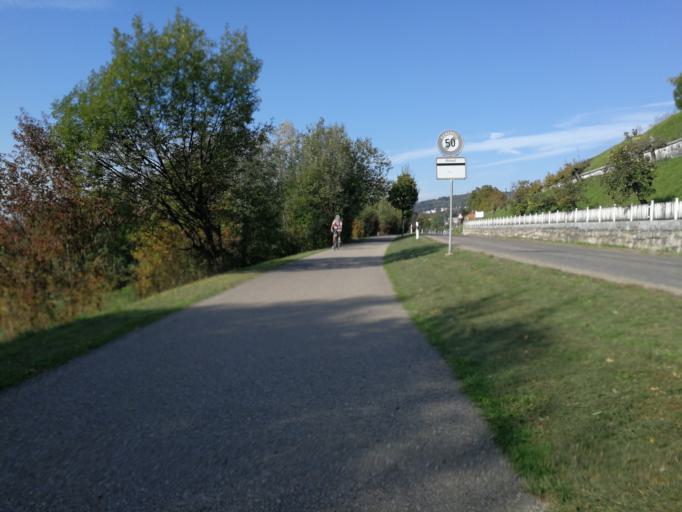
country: CH
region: Zurich
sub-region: Bezirk Hinwil
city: Hadlikon
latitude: 47.2907
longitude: 8.8534
